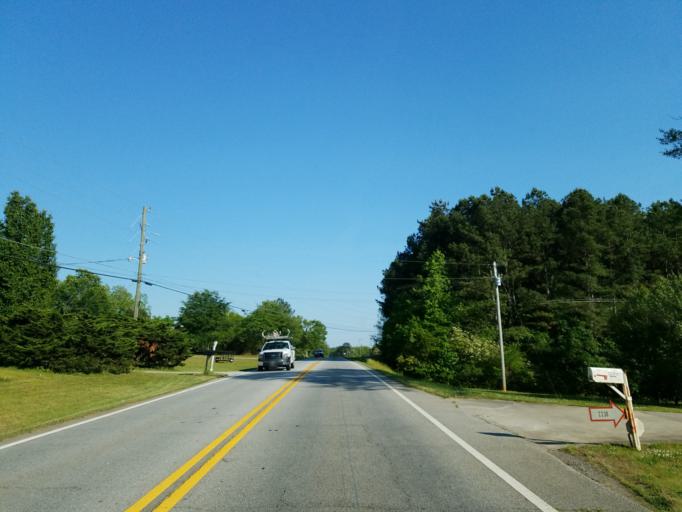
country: US
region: Georgia
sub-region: Carroll County
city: Villa Rica
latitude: 33.7726
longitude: -84.9608
